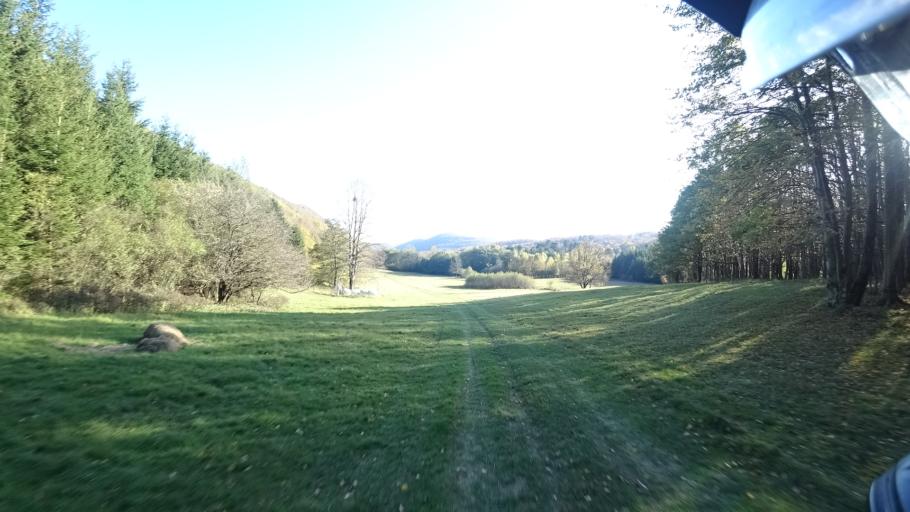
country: HR
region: Primorsko-Goranska
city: Klana
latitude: 45.4889
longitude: 14.4091
